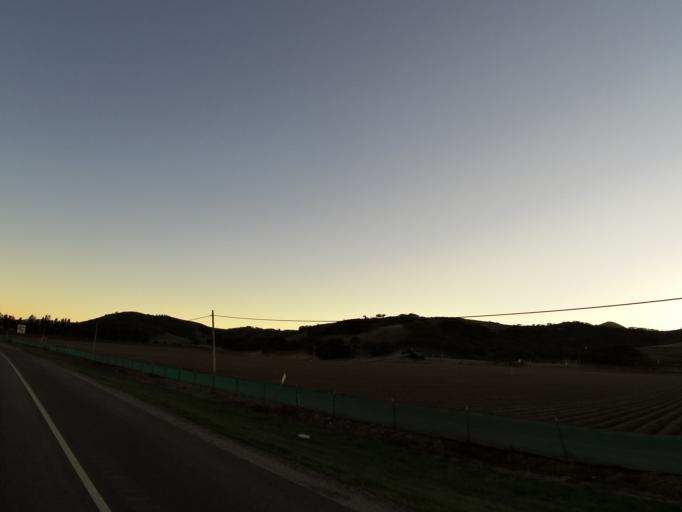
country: US
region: California
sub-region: Monterey County
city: King City
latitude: 36.2182
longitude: -121.1675
